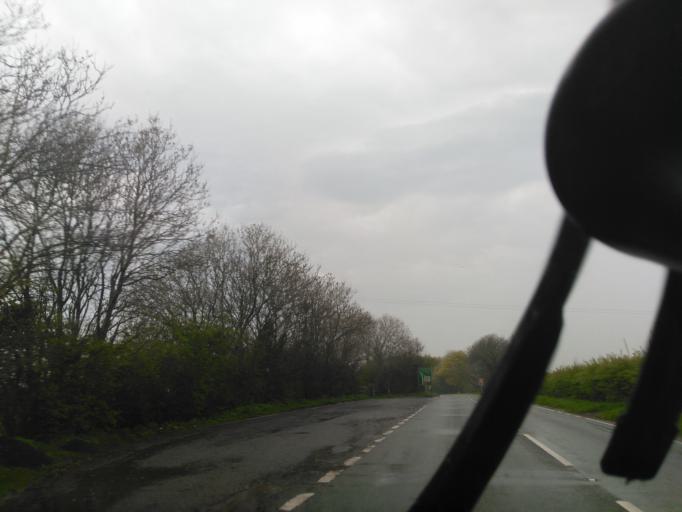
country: GB
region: England
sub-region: Somerset
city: Shepton Mallet
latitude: 51.1705
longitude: -2.5695
